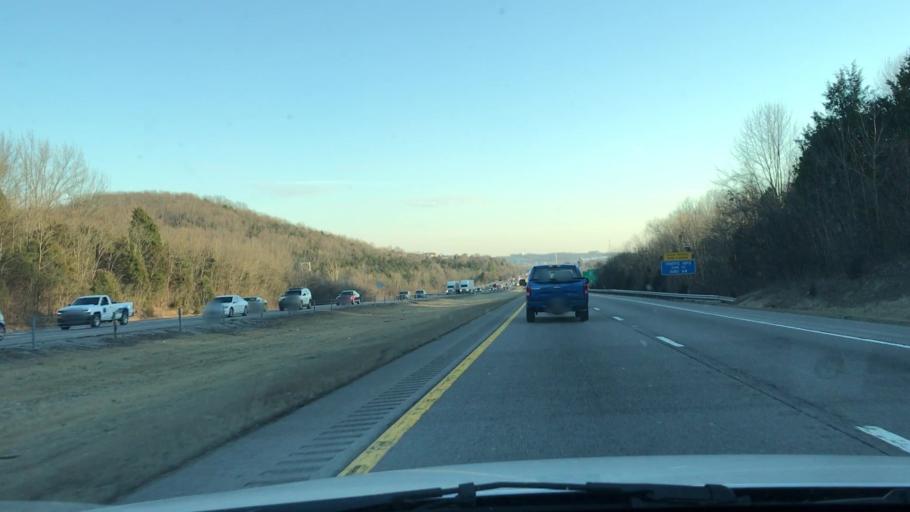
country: US
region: Tennessee
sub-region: Sumner County
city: Millersville
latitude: 36.3528
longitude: -86.7194
